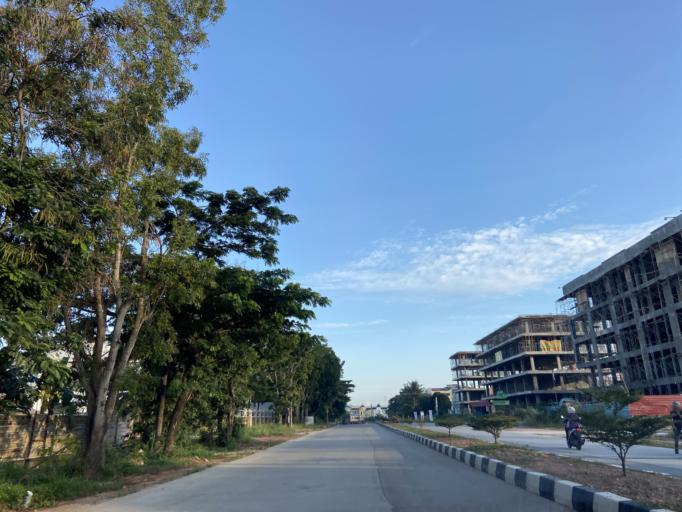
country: SG
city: Singapore
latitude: 1.1271
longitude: 104.0402
